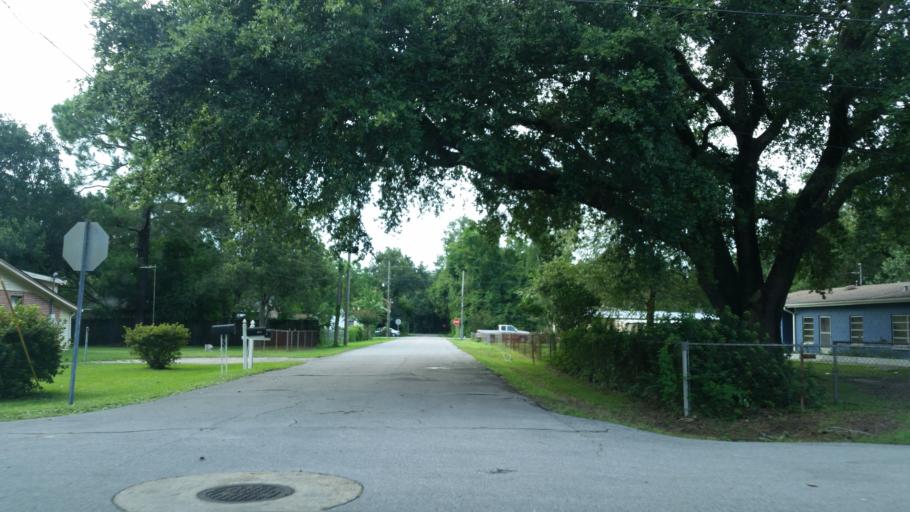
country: US
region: Florida
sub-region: Escambia County
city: Ferry Pass
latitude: 30.5139
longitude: -87.2140
